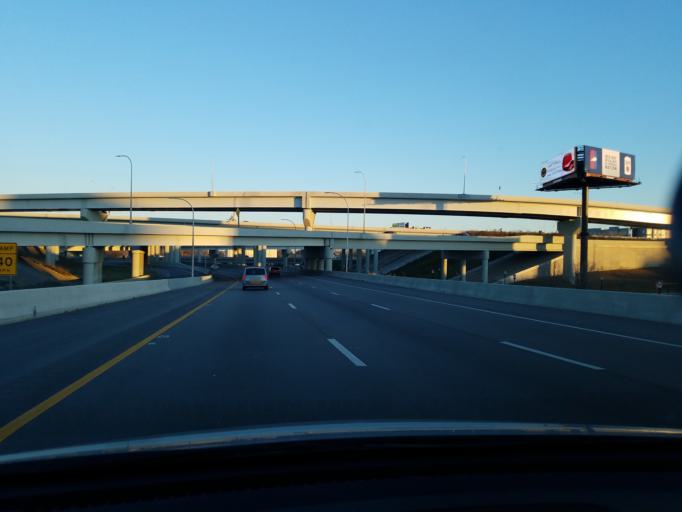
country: US
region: Kentucky
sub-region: Jefferson County
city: Louisville
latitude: 38.2580
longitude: -85.7435
